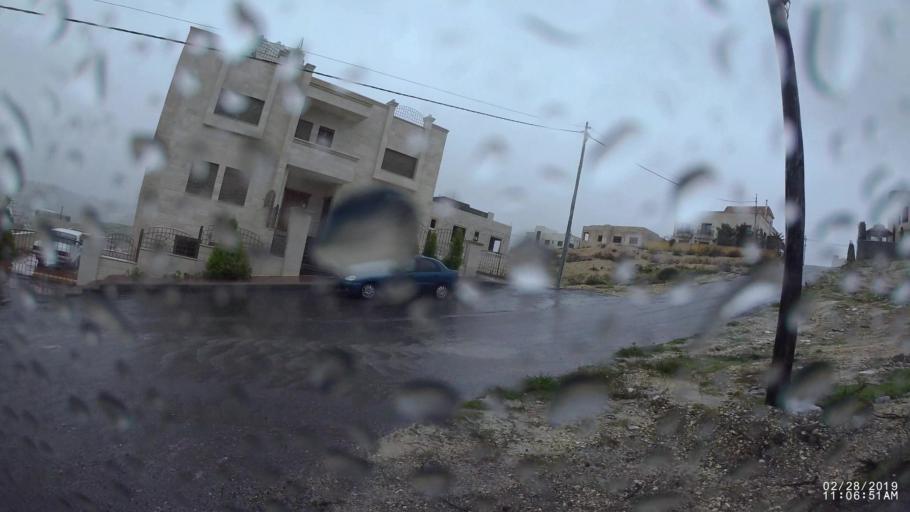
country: JO
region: Amman
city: Al Jubayhah
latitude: 32.0127
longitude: 35.9014
